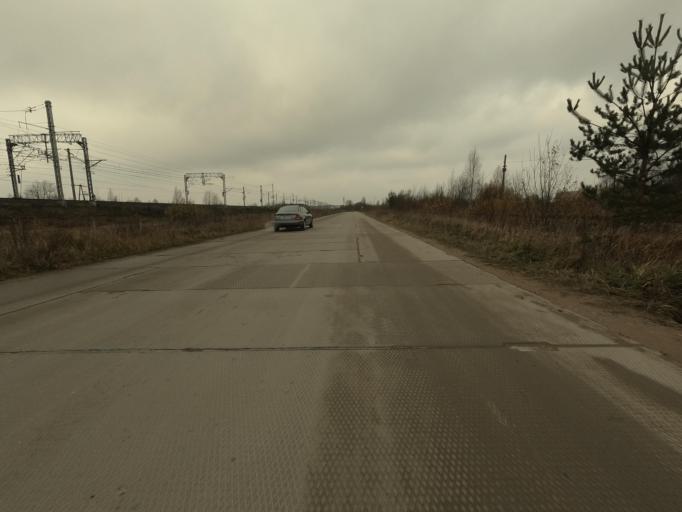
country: RU
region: Leningrad
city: Lyuban'
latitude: 59.4769
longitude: 31.2572
